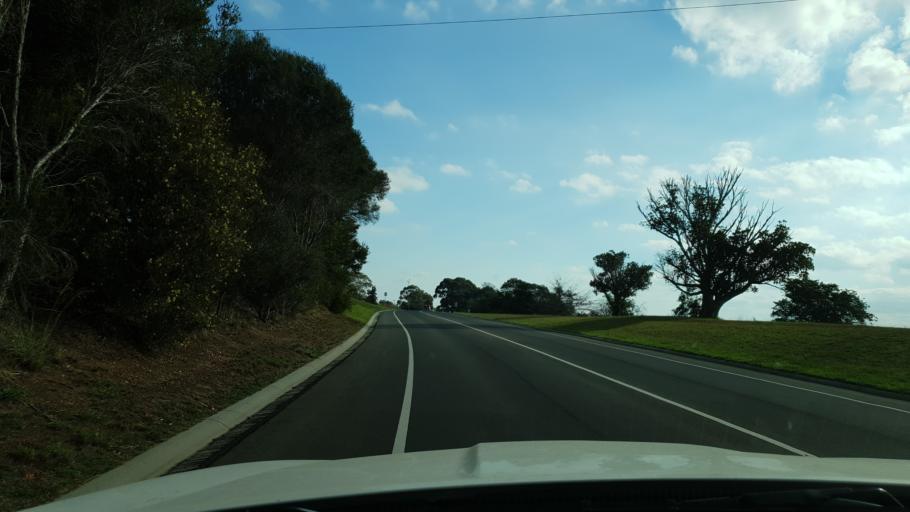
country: AU
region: Victoria
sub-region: East Gippsland
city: Bairnsdale
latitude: -37.8167
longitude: 147.6118
